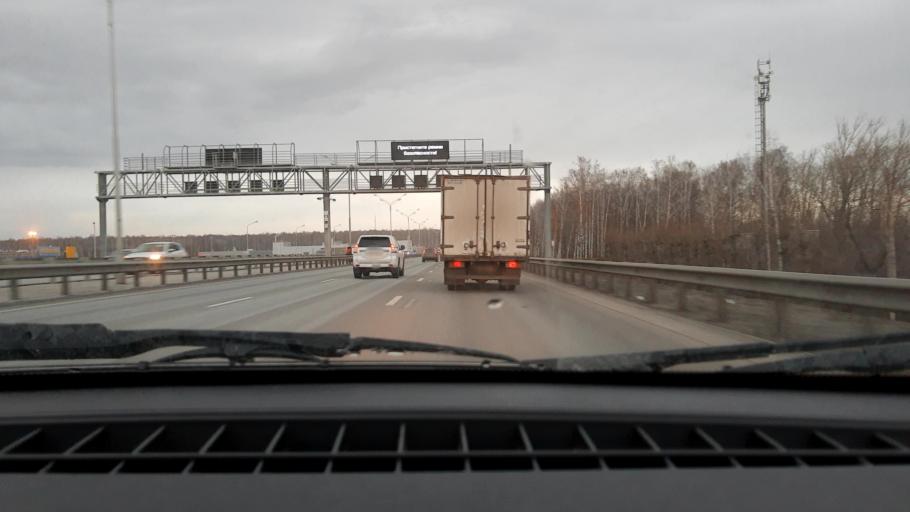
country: RU
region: Bashkortostan
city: Ufa
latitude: 54.6768
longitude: 55.9336
